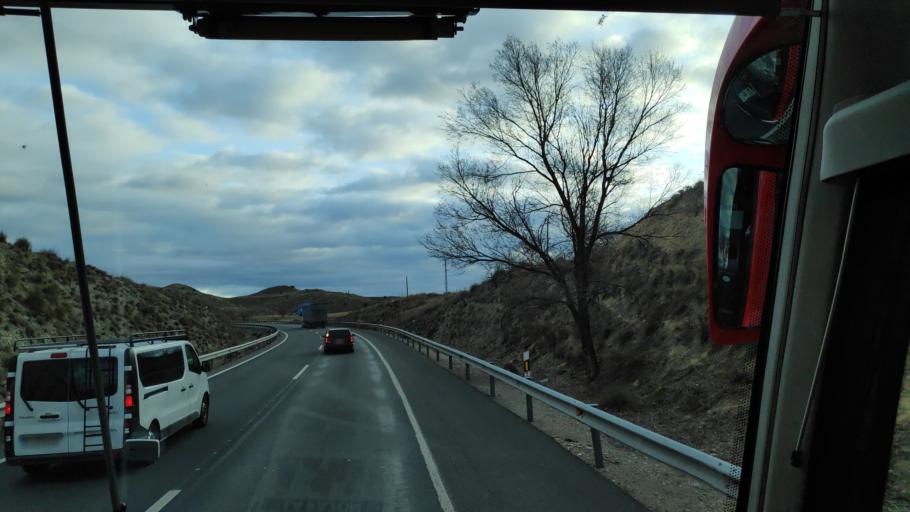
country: ES
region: Madrid
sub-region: Provincia de Madrid
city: Perales de Tajuna
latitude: 40.2179
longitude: -3.3299
